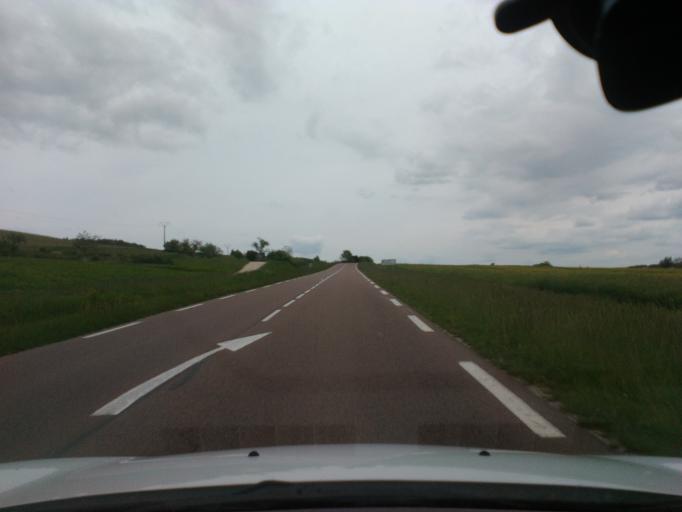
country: FR
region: Champagne-Ardenne
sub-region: Departement de l'Aube
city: Bar-sur-Aube
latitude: 48.2576
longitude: 4.6764
